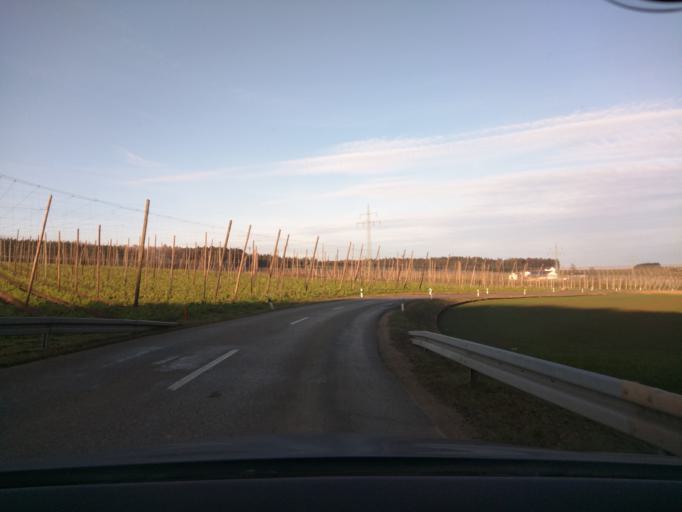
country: DE
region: Bavaria
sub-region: Upper Bavaria
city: Wolnzach
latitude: 48.5773
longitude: 11.6700
